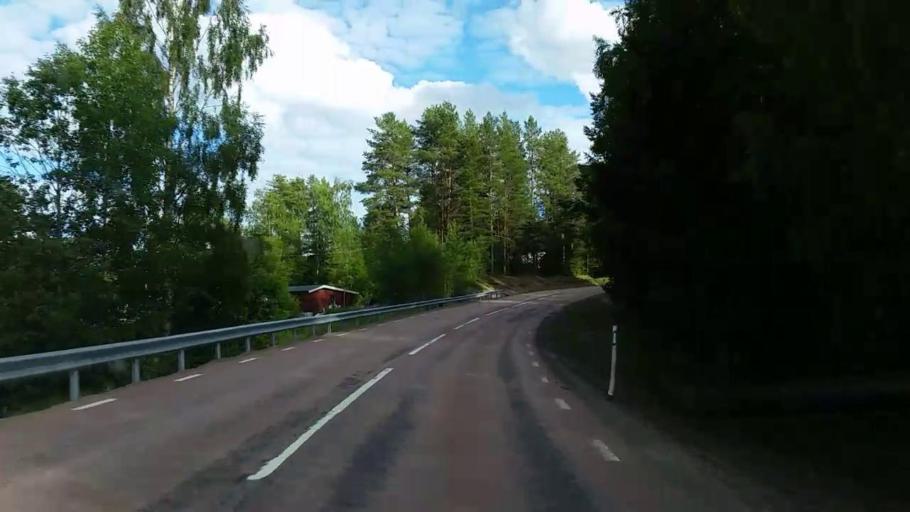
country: SE
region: Gaevleborg
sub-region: Ljusdals Kommun
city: Farila
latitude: 61.8957
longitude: 15.9064
